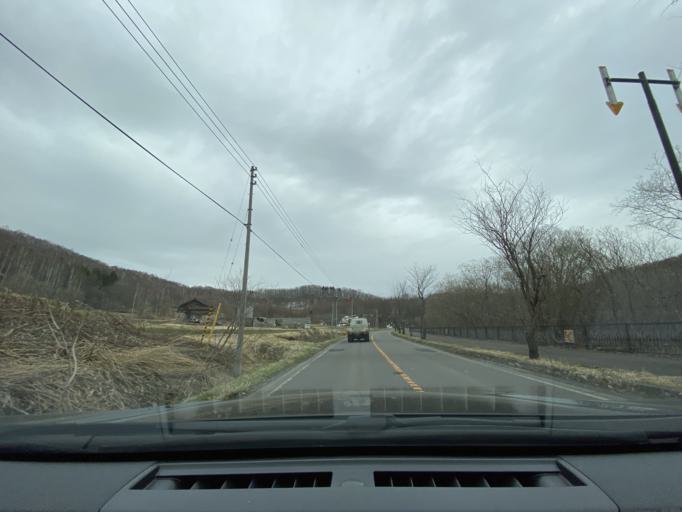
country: JP
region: Hokkaido
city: Nayoro
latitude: 44.0945
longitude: 142.4378
